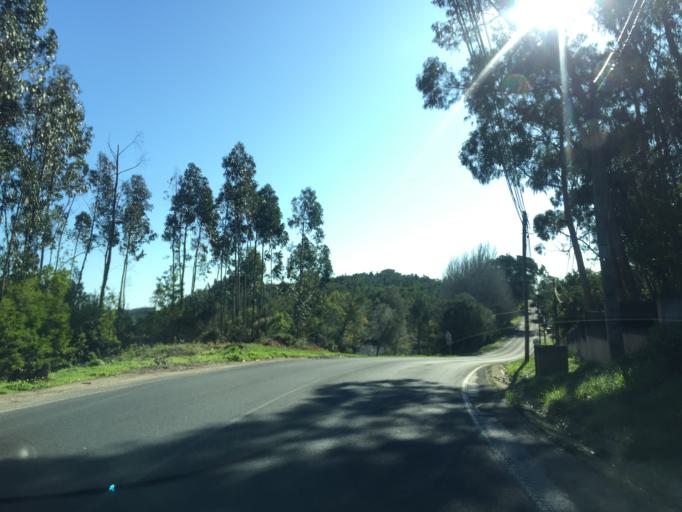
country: PT
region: Lisbon
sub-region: Sintra
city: Belas
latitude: 38.7982
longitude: -9.2696
